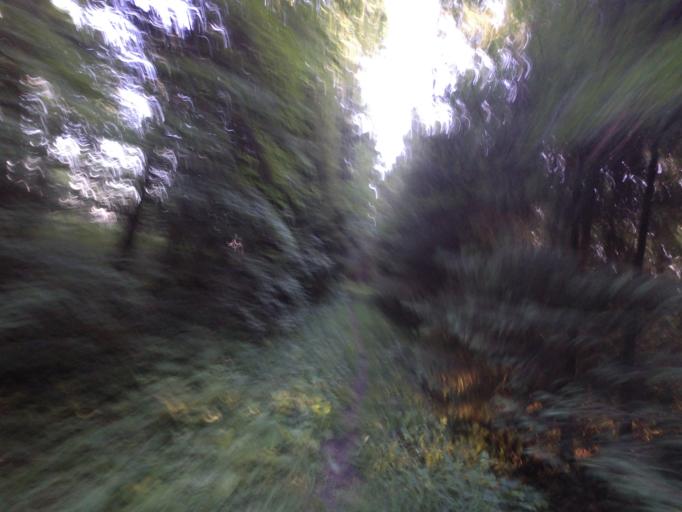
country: AT
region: Salzburg
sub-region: Politischer Bezirk Hallein
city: Puch bei Hallein
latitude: 47.7150
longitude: 13.0796
